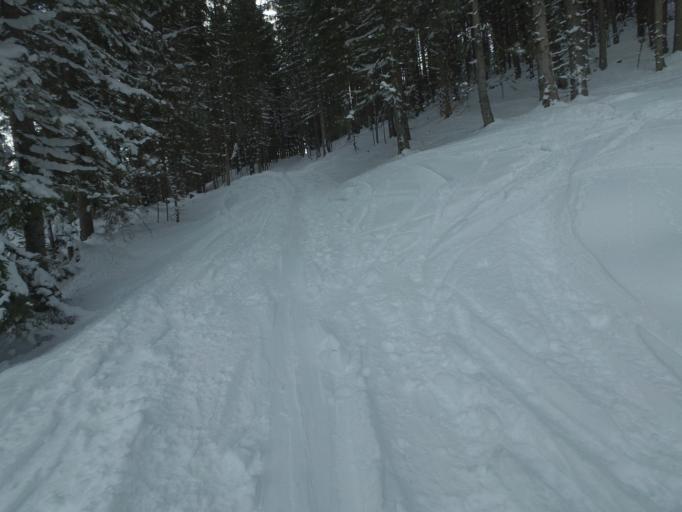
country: AT
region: Salzburg
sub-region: Politischer Bezirk Zell am See
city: Lend
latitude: 47.2790
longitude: 13.0125
